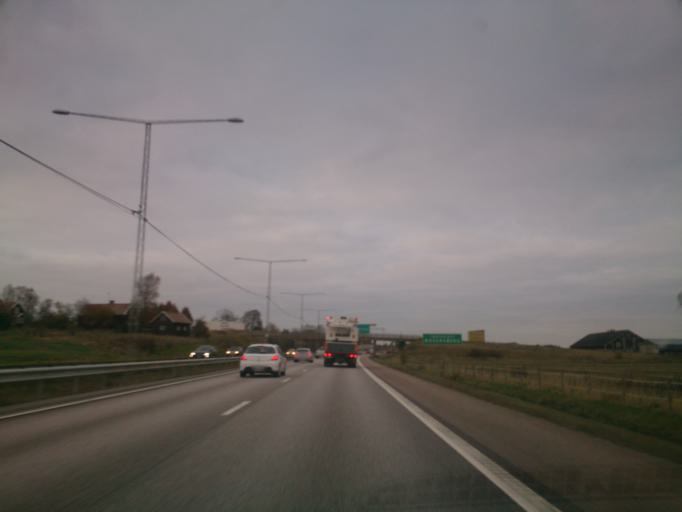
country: SE
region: Stockholm
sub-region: Sigtuna Kommun
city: Rosersberg
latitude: 59.5662
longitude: 17.8976
